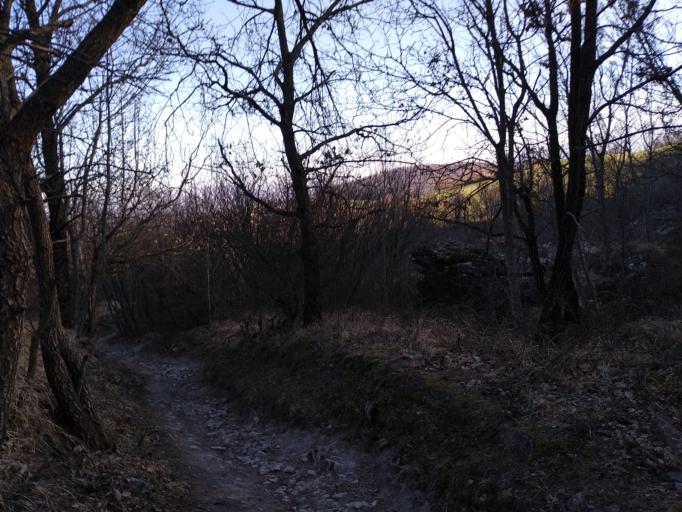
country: IT
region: Emilia-Romagna
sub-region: Provincia di Reggio Emilia
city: Castelnovo ne'Monti
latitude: 44.4239
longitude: 10.4203
